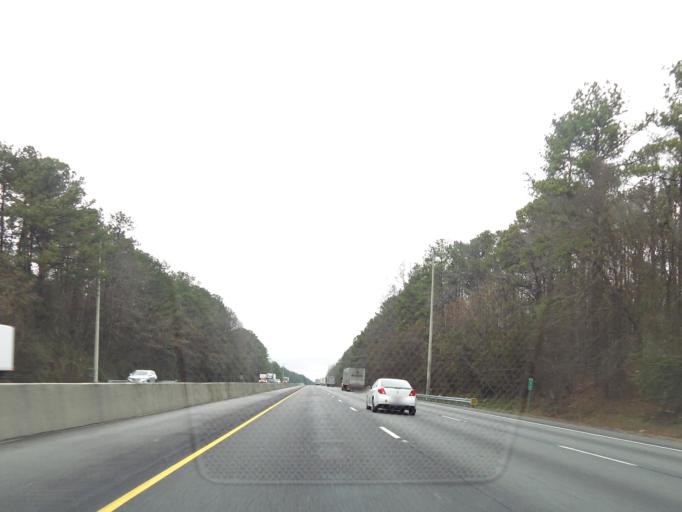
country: US
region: Georgia
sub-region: Bibb County
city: West Point
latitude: 32.9028
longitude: -83.7882
